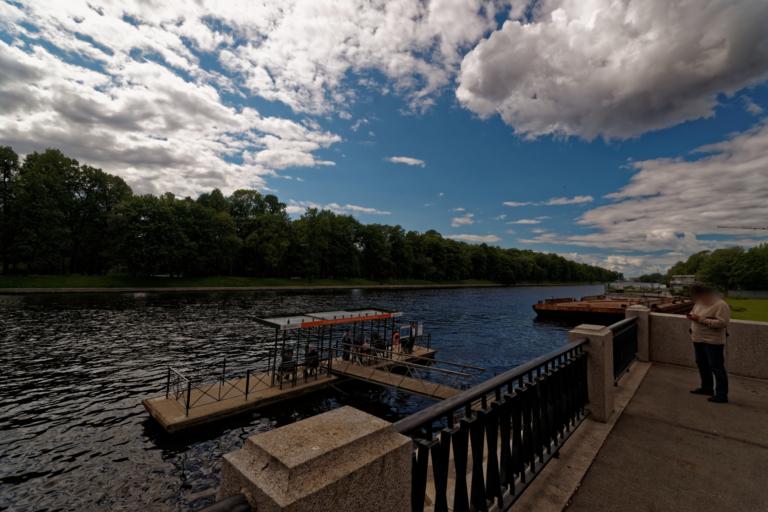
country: RU
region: St.-Petersburg
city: Staraya Derevnya
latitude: 59.9828
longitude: 30.2533
